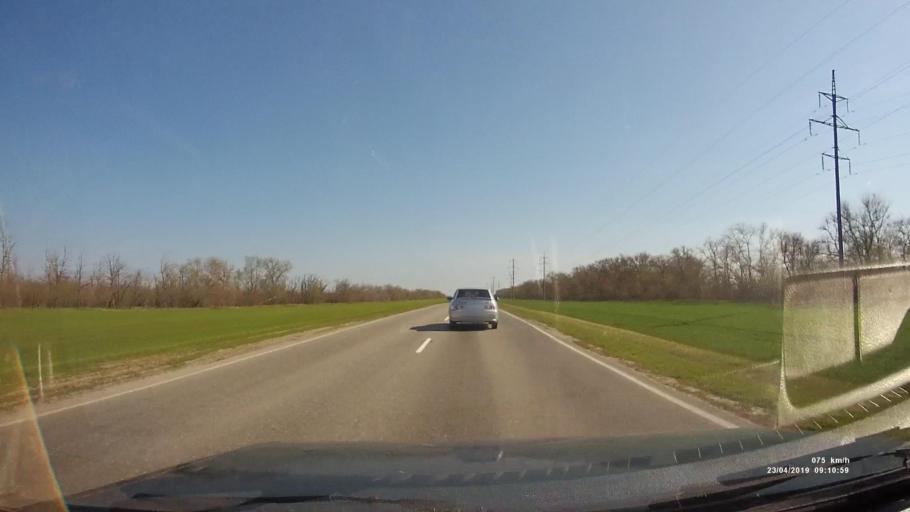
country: RU
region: Rostov
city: Sal'sk
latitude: 46.5916
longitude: 41.6248
